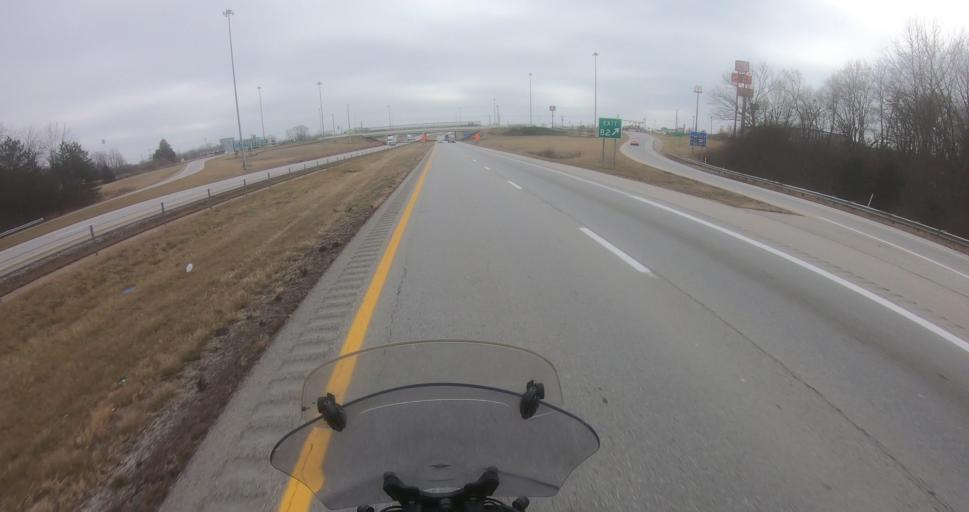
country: US
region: Ohio
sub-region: Miami County
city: Piqua
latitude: 40.1534
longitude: -84.2210
